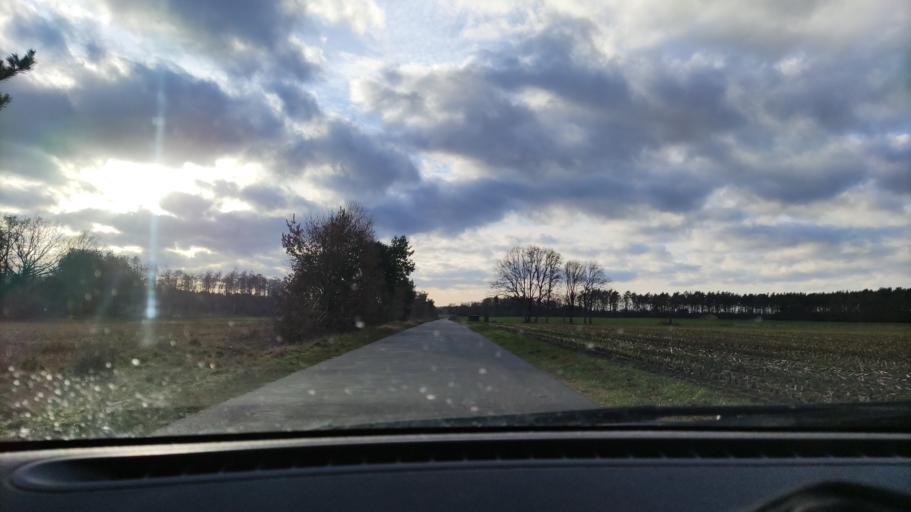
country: DE
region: Lower Saxony
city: Eimke
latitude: 52.9788
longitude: 10.3299
